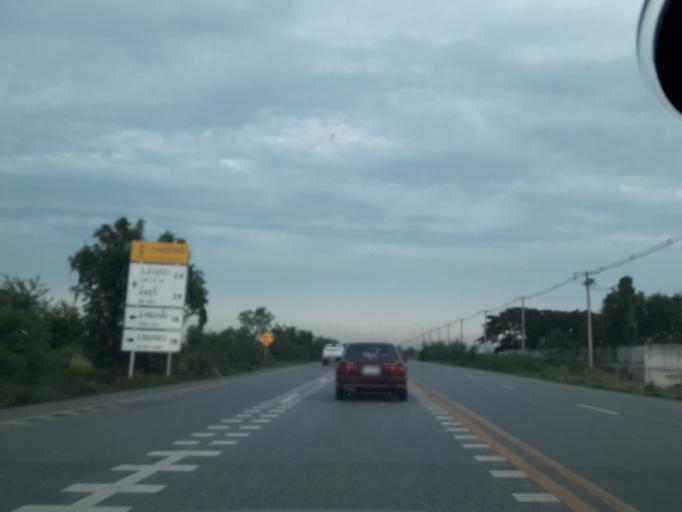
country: TH
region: Pathum Thani
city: Nong Suea
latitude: 14.1414
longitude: 100.7473
